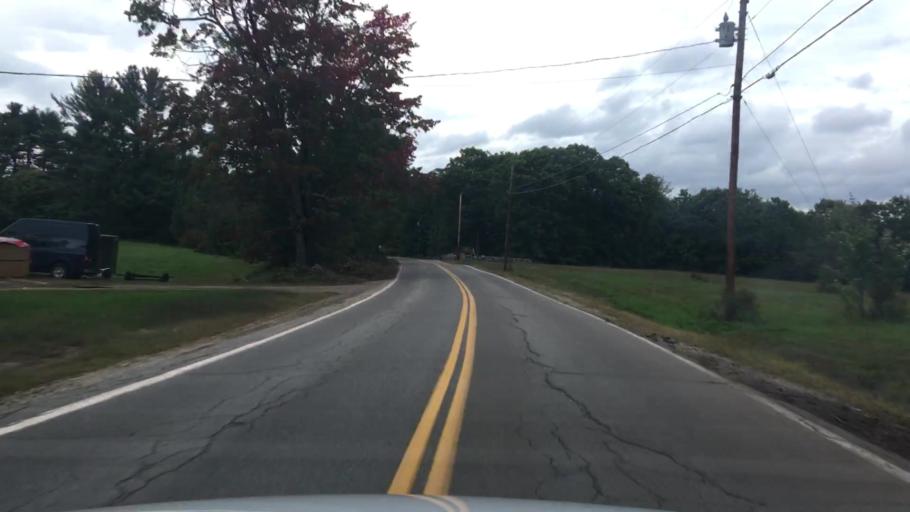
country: US
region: New Hampshire
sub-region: Carroll County
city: Effingham
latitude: 43.7679
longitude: -70.9972
